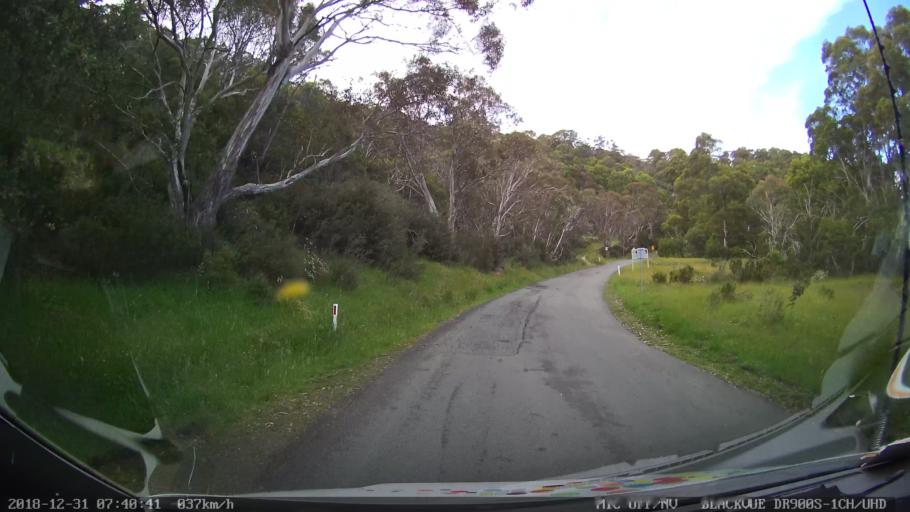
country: AU
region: New South Wales
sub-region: Snowy River
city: Jindabyne
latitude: -36.3518
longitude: 148.4160
